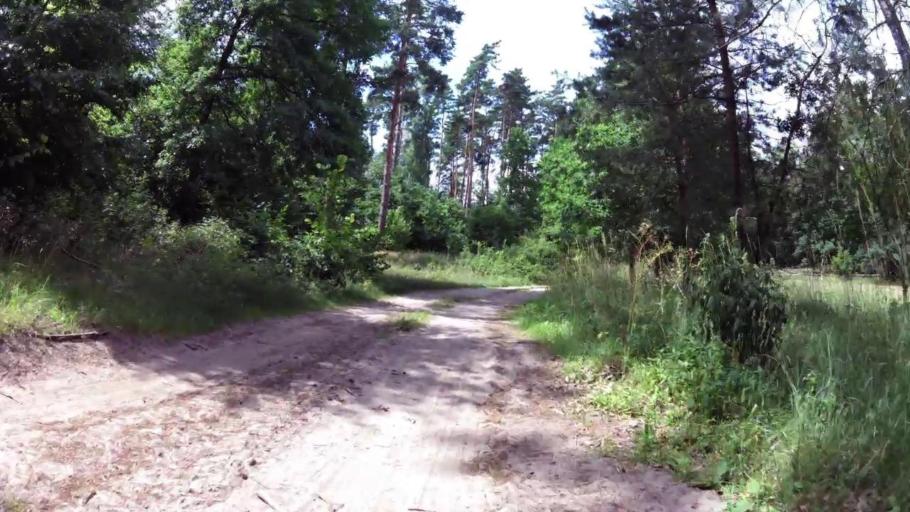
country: PL
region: West Pomeranian Voivodeship
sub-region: Powiat lobeski
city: Lobez
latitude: 53.5527
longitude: 15.6746
